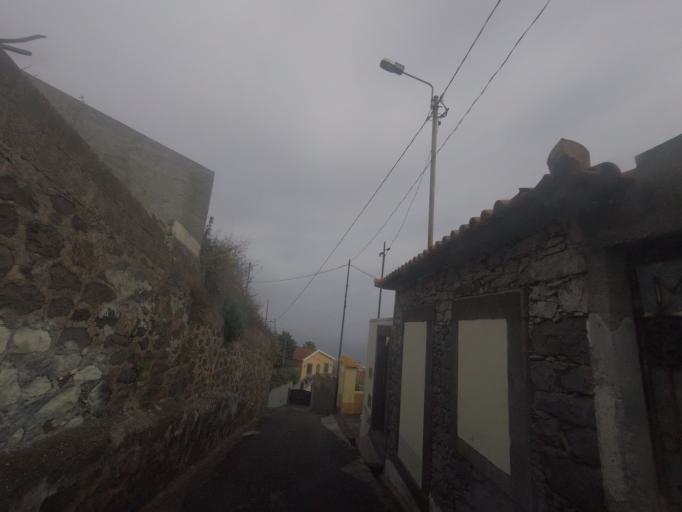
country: PT
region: Madeira
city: Camara de Lobos
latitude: 32.6710
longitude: -16.9482
